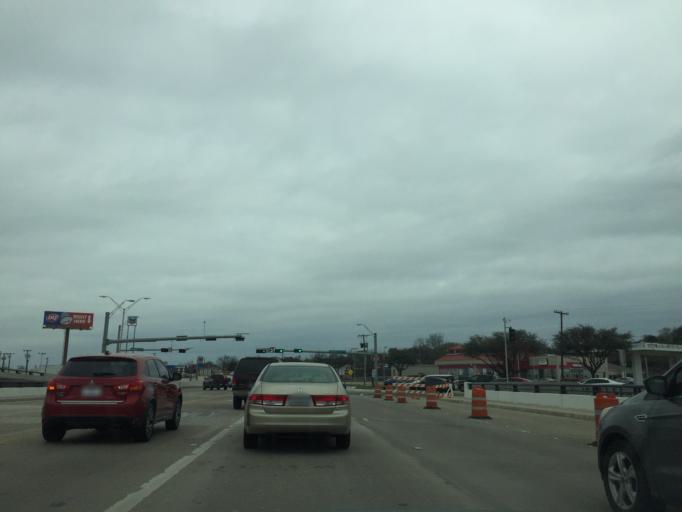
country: US
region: Texas
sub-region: Bell County
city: Harker Heights
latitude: 31.0708
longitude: -97.6696
